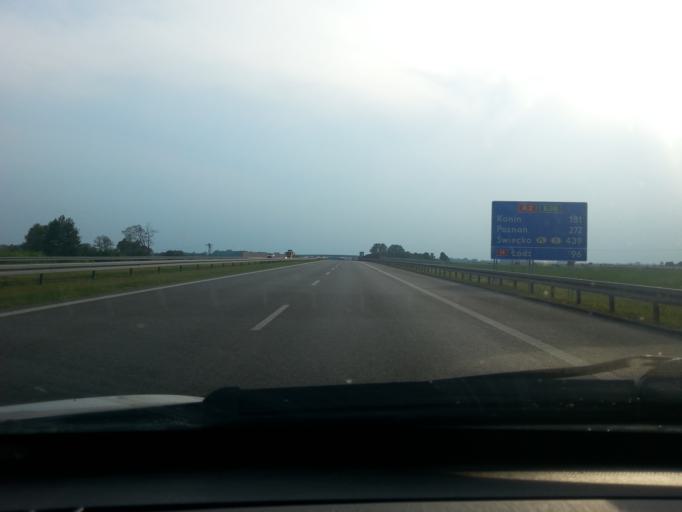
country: PL
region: Masovian Voivodeship
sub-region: Powiat grodziski
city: Grodzisk Mazowiecki
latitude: 52.1447
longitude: 20.6068
